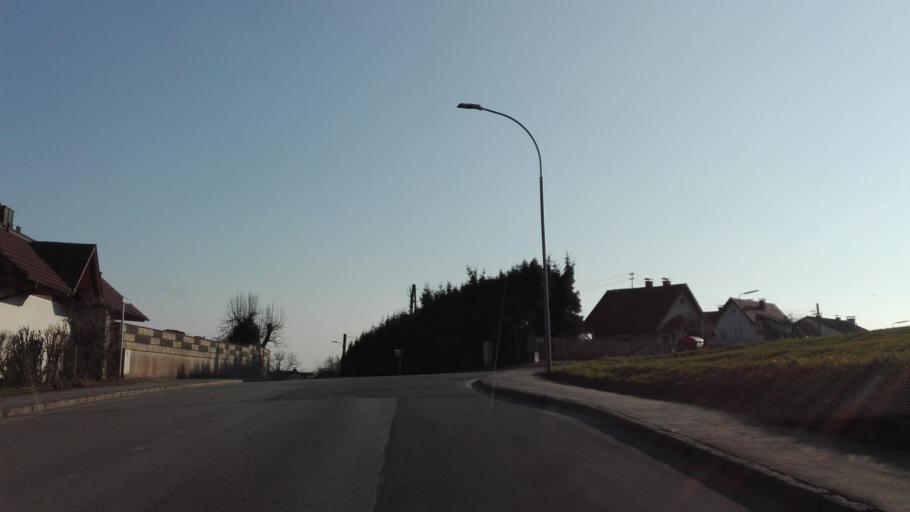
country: AT
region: Upper Austria
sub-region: Politischer Bezirk Linz-Land
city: Leonding
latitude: 48.2911
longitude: 14.2528
